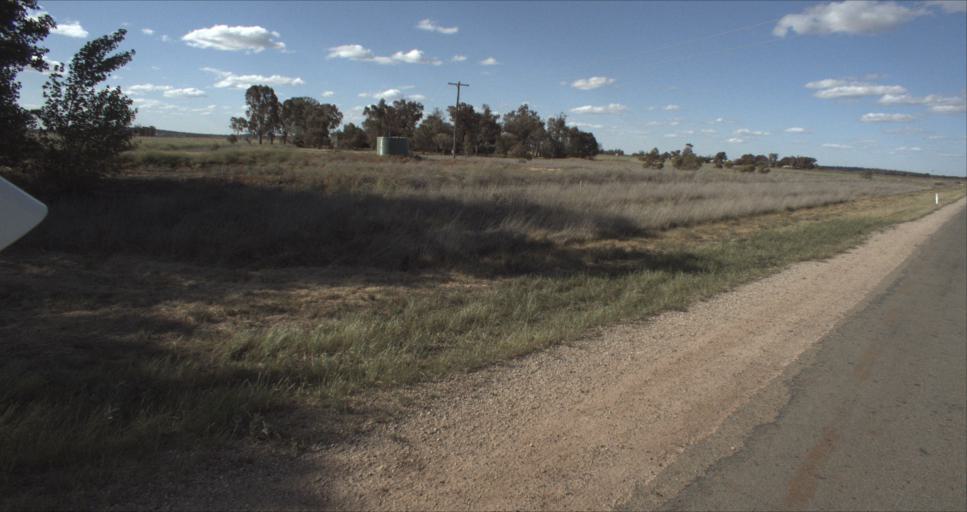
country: AU
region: New South Wales
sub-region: Leeton
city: Leeton
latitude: -34.4580
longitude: 146.2705
